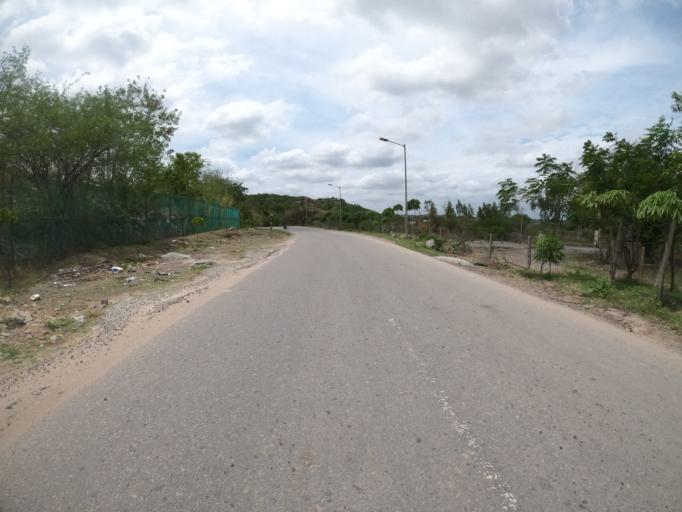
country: IN
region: Telangana
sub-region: Hyderabad
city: Hyderabad
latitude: 17.3124
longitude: 78.3739
